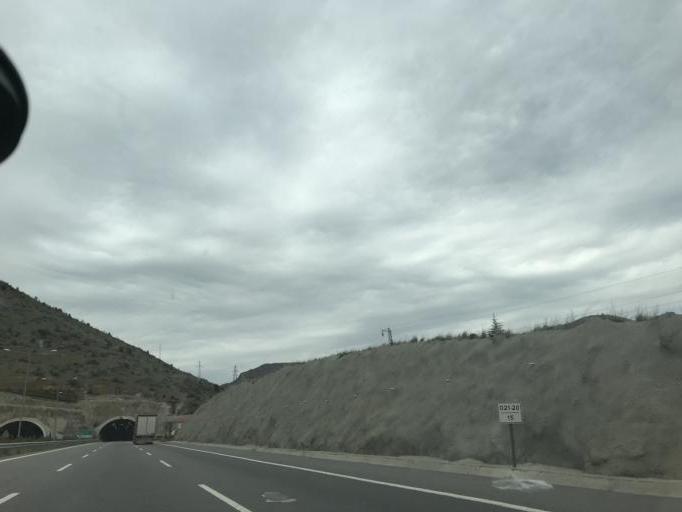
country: TR
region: Nigde
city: Ciftehan
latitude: 37.5726
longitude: 34.7535
